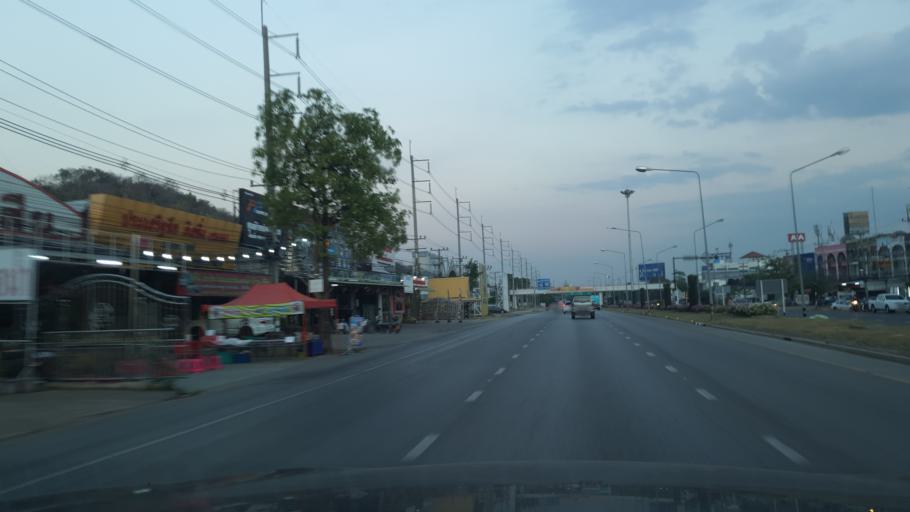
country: TH
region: Nakhon Sawan
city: Nakhon Sawan
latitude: 15.7070
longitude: 100.1063
